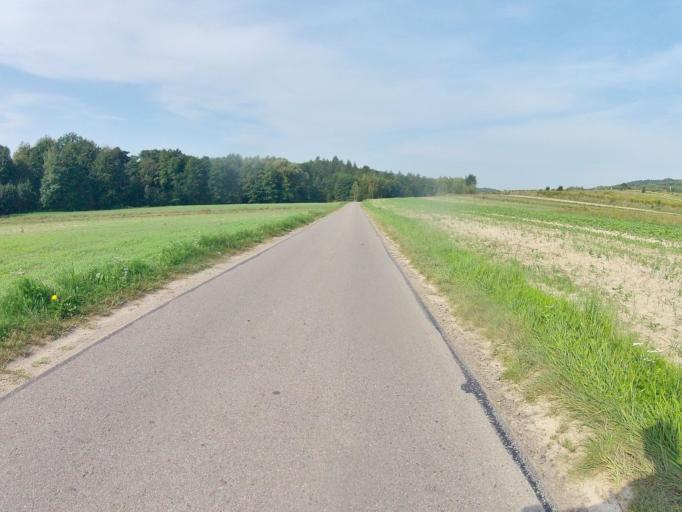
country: PL
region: Subcarpathian Voivodeship
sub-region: Powiat jasielski
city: Brzyska
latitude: 49.7923
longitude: 21.3950
